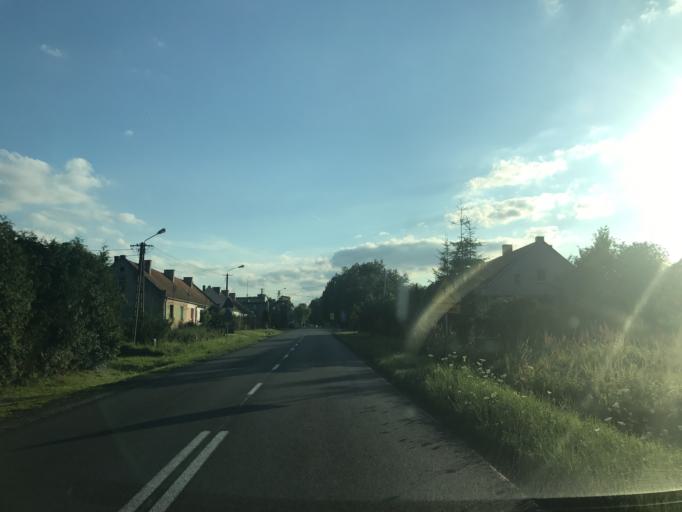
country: PL
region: Greater Poland Voivodeship
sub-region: Powiat jarocinski
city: Witaszyce
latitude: 52.0018
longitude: 17.5971
